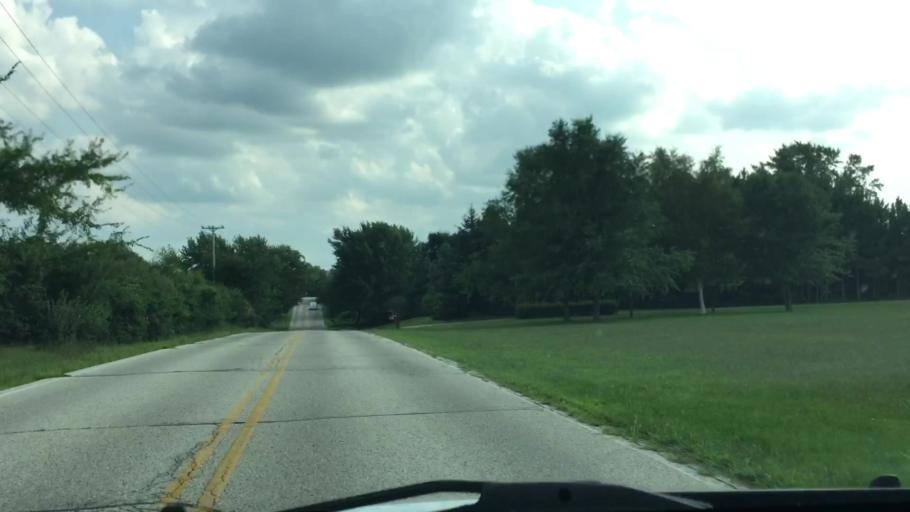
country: US
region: Wisconsin
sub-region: Waukesha County
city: Wales
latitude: 43.0235
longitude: -88.3643
